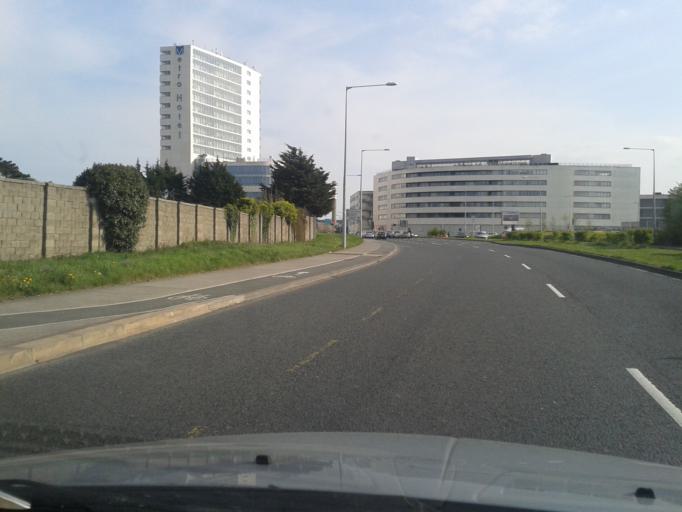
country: IE
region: Leinster
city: Ballymun
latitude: 53.4026
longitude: -6.2650
